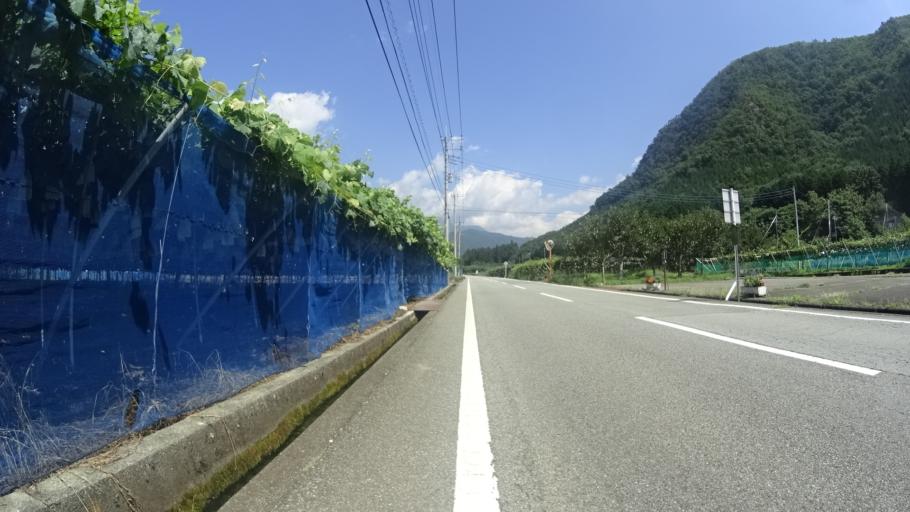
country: JP
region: Yamanashi
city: Enzan
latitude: 35.7320
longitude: 138.7223
